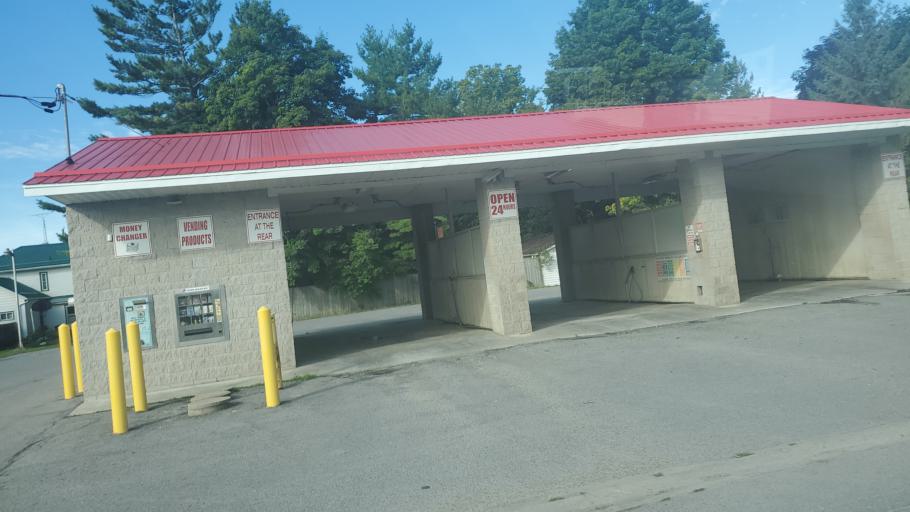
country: CA
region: Ontario
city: Belleville
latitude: 44.4780
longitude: -77.3106
